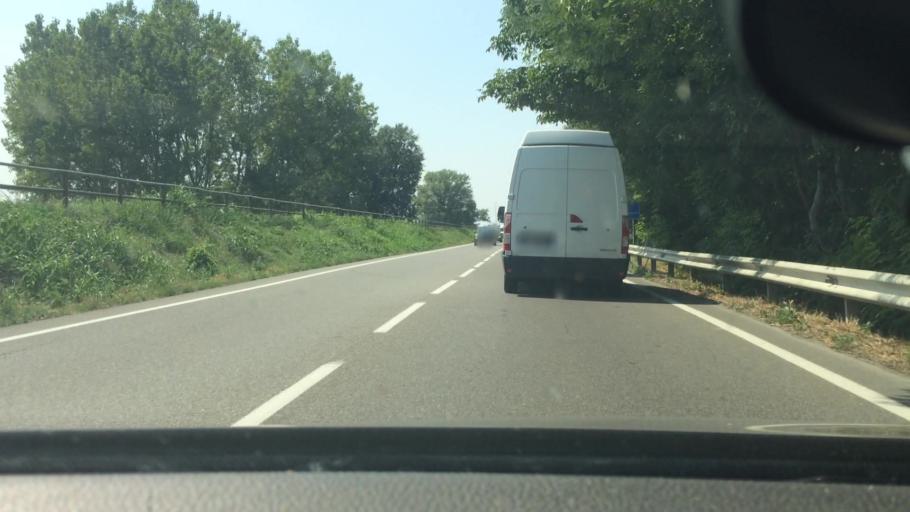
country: IT
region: Lombardy
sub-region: Provincia di Lodi
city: San Rocco al Porto
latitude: 45.0795
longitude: 9.6971
